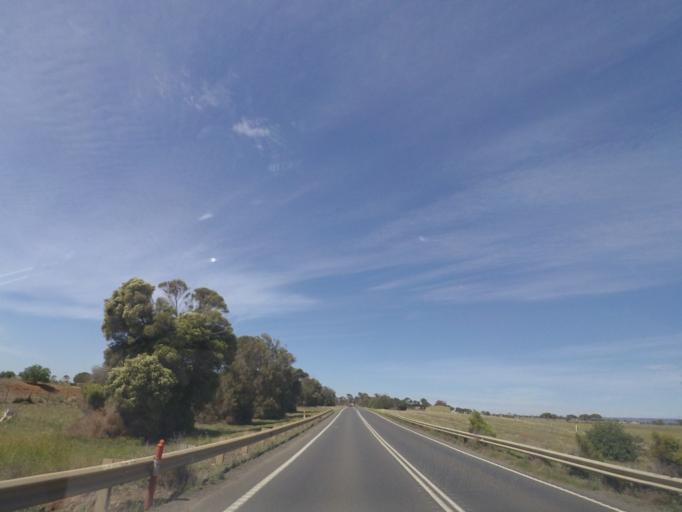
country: AU
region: Victoria
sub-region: Moorabool
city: Bacchus Marsh
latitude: -37.7159
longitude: 144.4525
